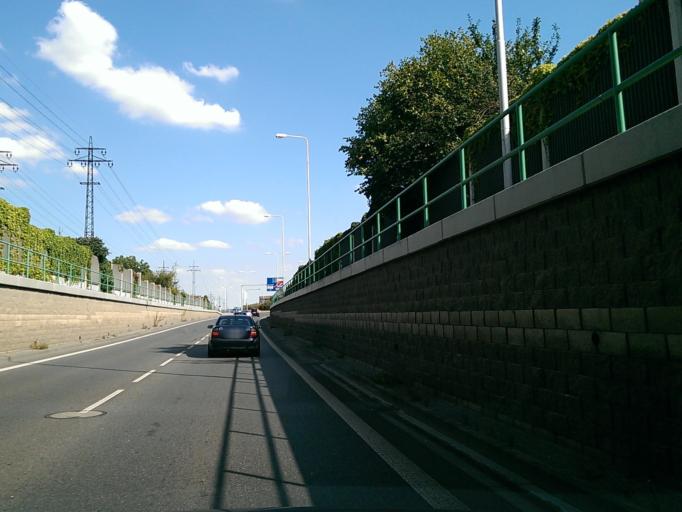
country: CZ
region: Central Bohemia
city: Kosmonosy
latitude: 50.4334
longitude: 14.9214
